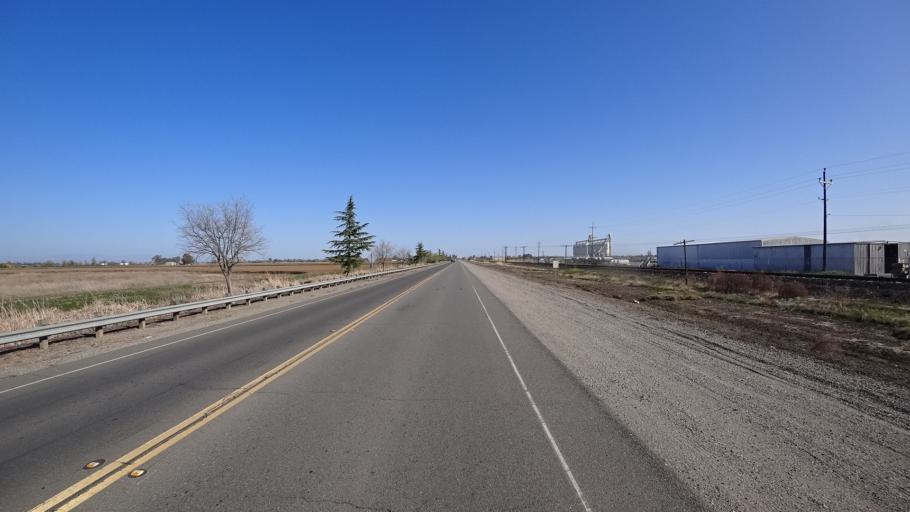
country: US
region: California
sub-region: Glenn County
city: Willows
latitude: 39.4963
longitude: -122.1932
